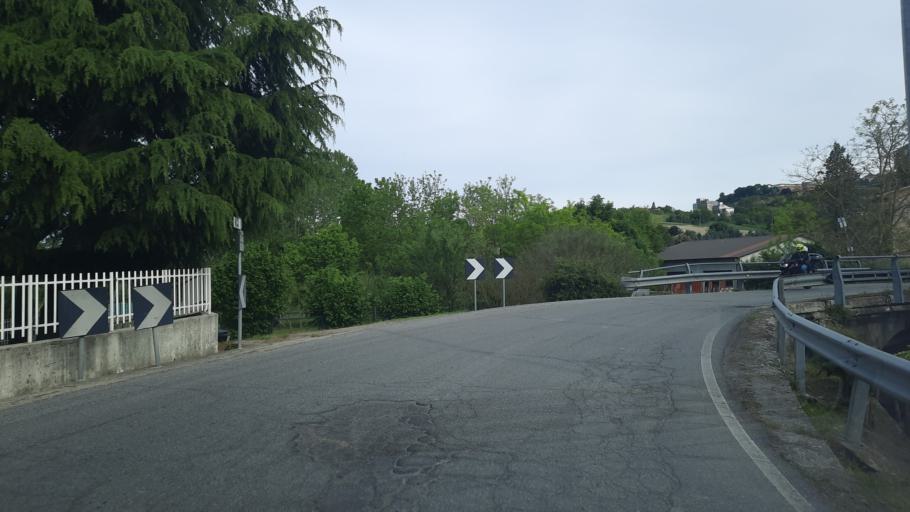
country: IT
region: Piedmont
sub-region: Provincia di Asti
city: Moncalvo
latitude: 45.0616
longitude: 8.2600
